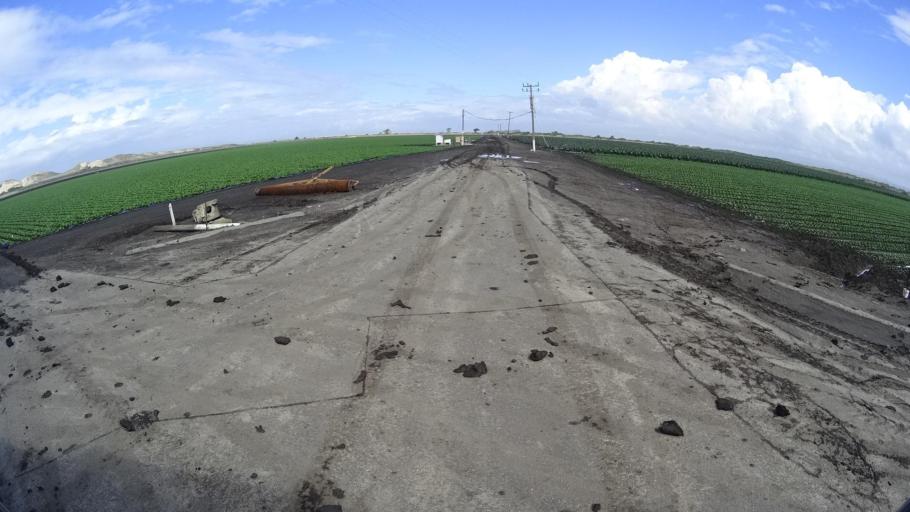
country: US
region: California
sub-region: Monterey County
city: Marina
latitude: 36.7279
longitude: -121.7921
